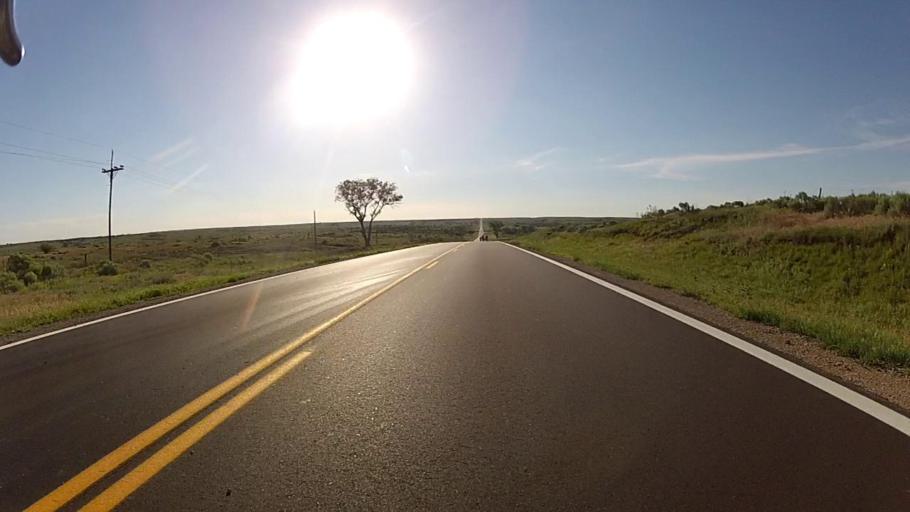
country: US
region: Kansas
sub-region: Comanche County
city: Coldwater
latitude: 37.2815
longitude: -99.0552
